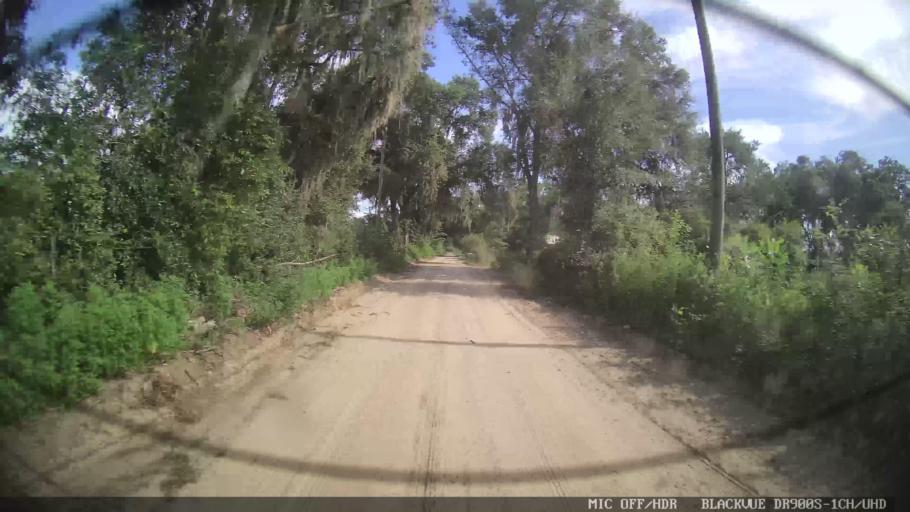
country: US
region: Georgia
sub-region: Echols County
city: Statenville
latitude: 30.6252
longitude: -83.1870
